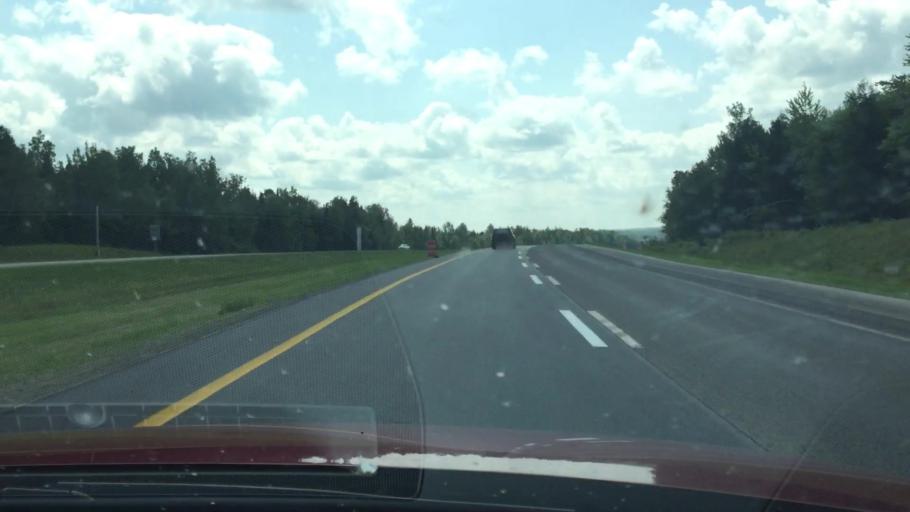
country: US
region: Maine
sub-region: Penobscot County
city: Medway
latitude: 45.6172
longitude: -68.5104
